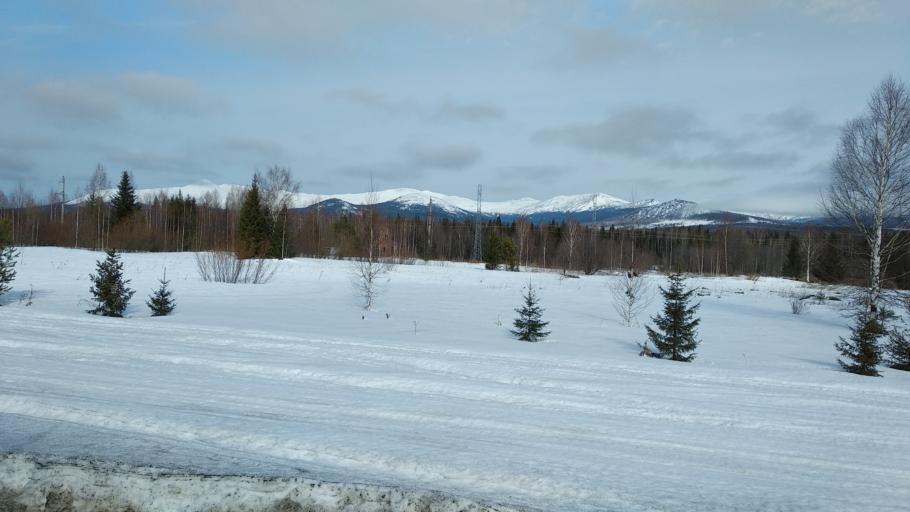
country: RU
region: Sverdlovsk
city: Karpinsk
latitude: 59.5275
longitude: 59.2528
